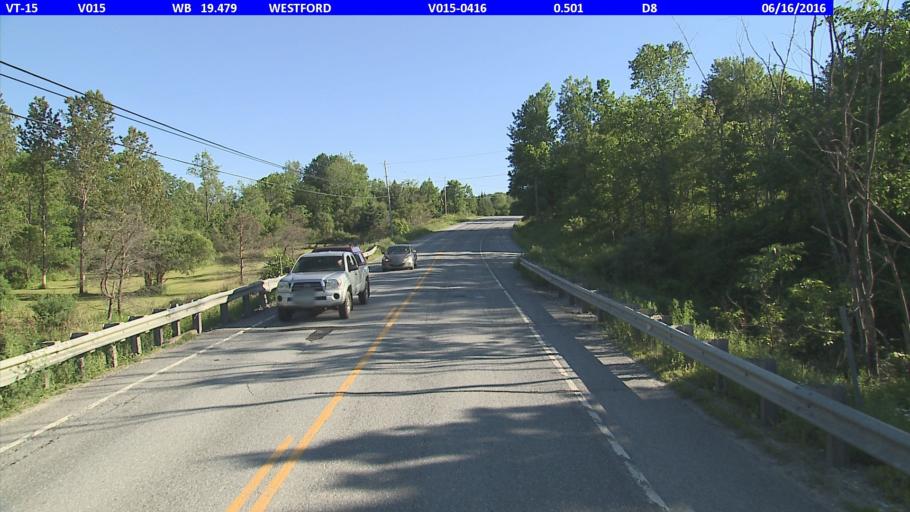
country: US
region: Vermont
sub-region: Chittenden County
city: Jericho
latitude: 44.6013
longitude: -72.9345
